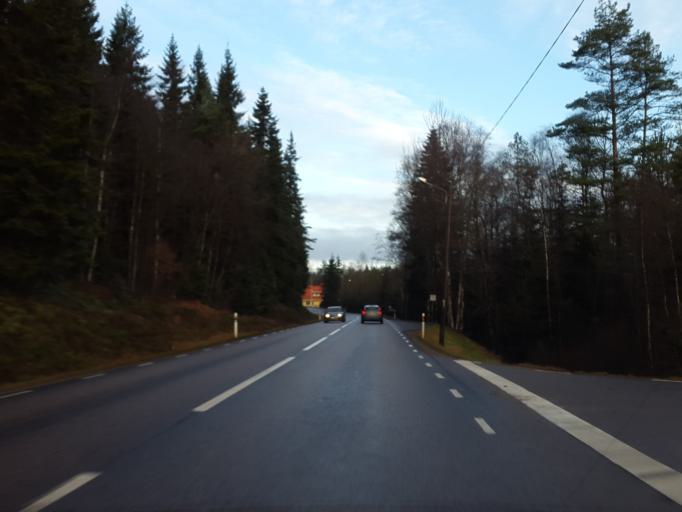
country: SE
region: Vaestra Goetaland
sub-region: Boras Kommun
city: Sjomarken
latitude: 57.7529
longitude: 12.8828
